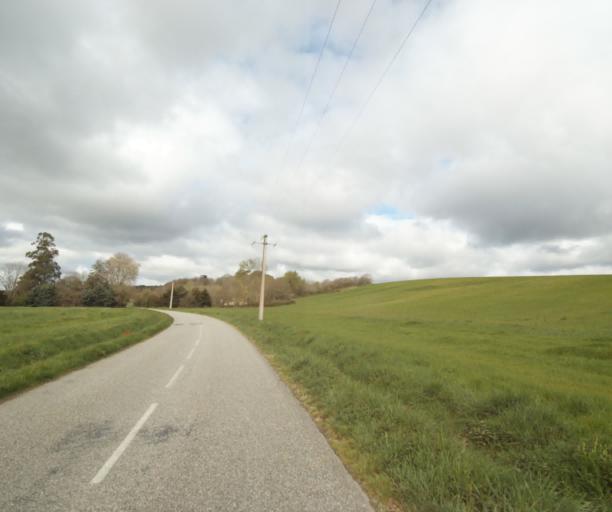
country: FR
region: Midi-Pyrenees
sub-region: Departement de l'Ariege
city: Saverdun
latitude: 43.2273
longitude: 1.5550
